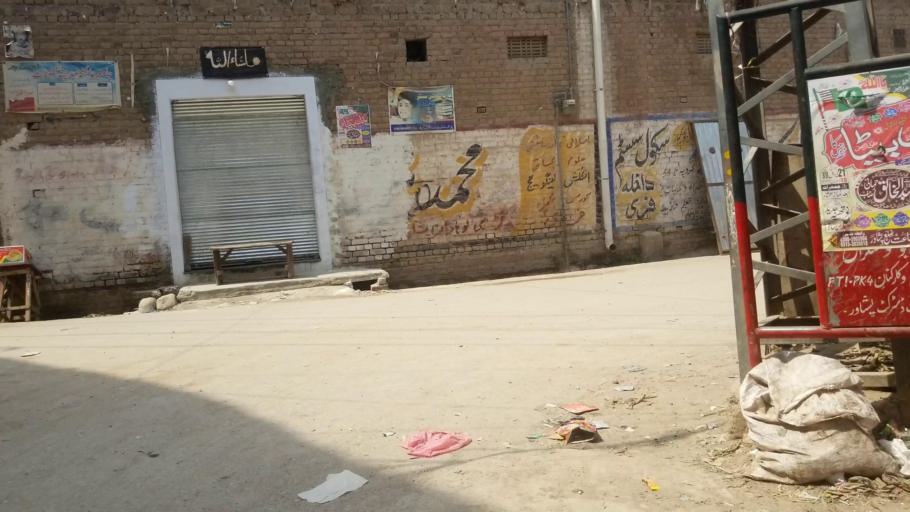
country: PK
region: Khyber Pakhtunkhwa
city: Peshawar
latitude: 33.9840
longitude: 71.5397
